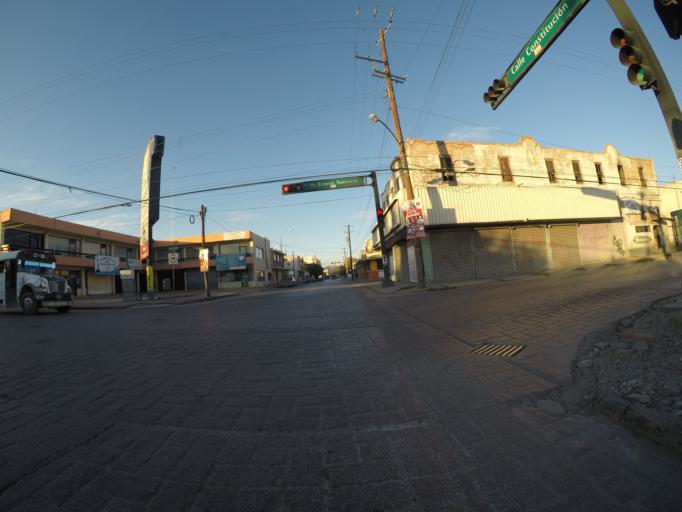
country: MX
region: Chihuahua
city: Ciudad Juarez
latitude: 31.7357
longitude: -106.4779
